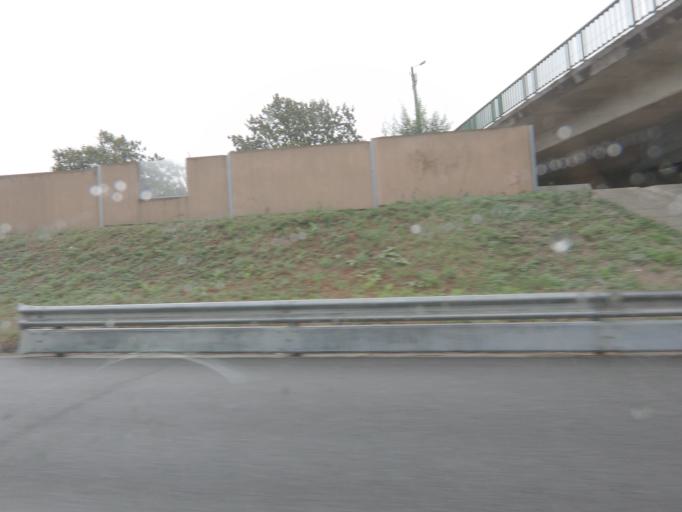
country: PT
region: Porto
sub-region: Penafiel
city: Penafiel
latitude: 41.2084
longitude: -8.2918
